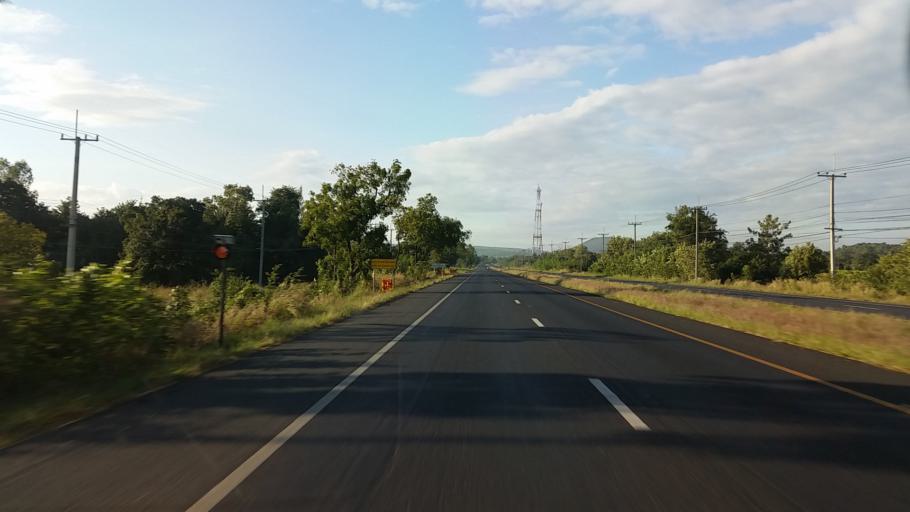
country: TH
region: Lop Buri
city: Phatthana Nikhom
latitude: 15.0037
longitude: 100.9394
